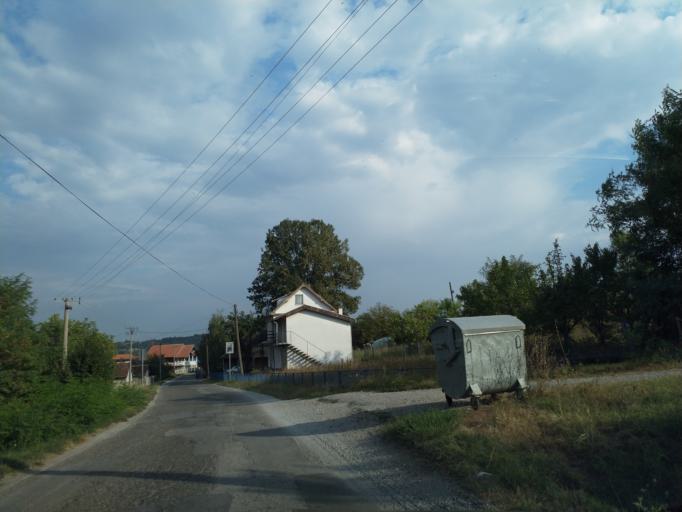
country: RS
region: Central Serbia
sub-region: Pomoravski Okrug
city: Paracin
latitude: 43.8419
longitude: 21.4730
